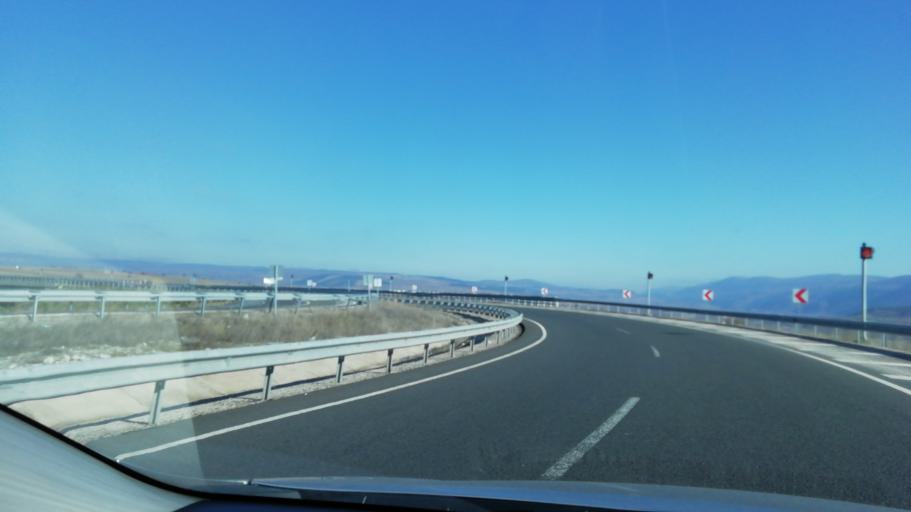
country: TR
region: Karabuk
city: Gozyeri
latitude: 40.8702
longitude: 32.5778
